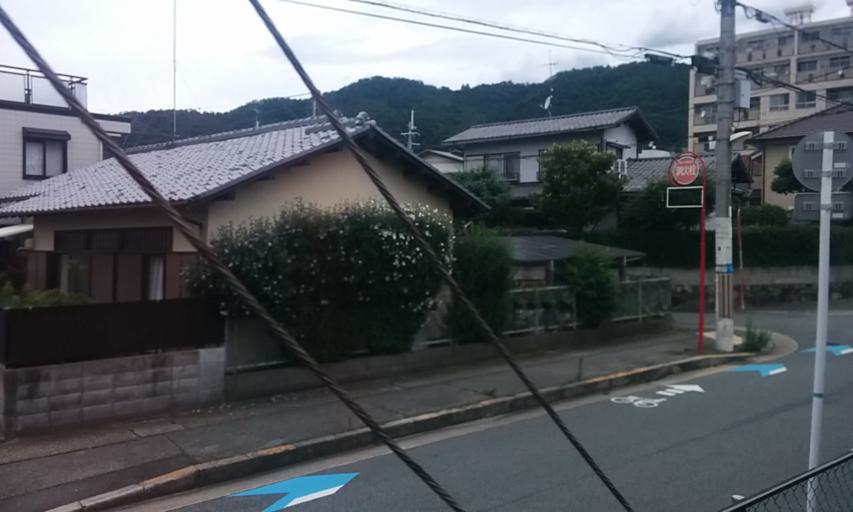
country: JP
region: Osaka
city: Mino
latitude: 34.8314
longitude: 135.4676
